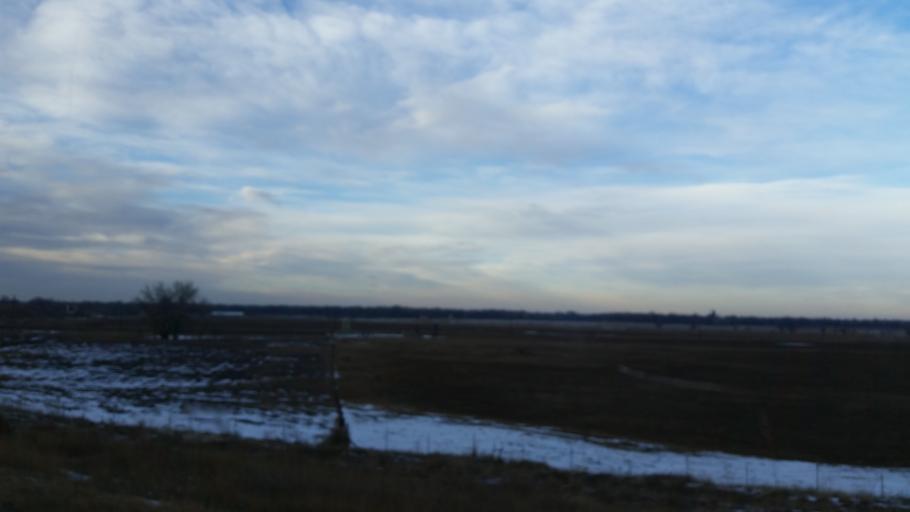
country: US
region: Colorado
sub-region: Weld County
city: Kersey
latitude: 40.3889
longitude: -104.5436
